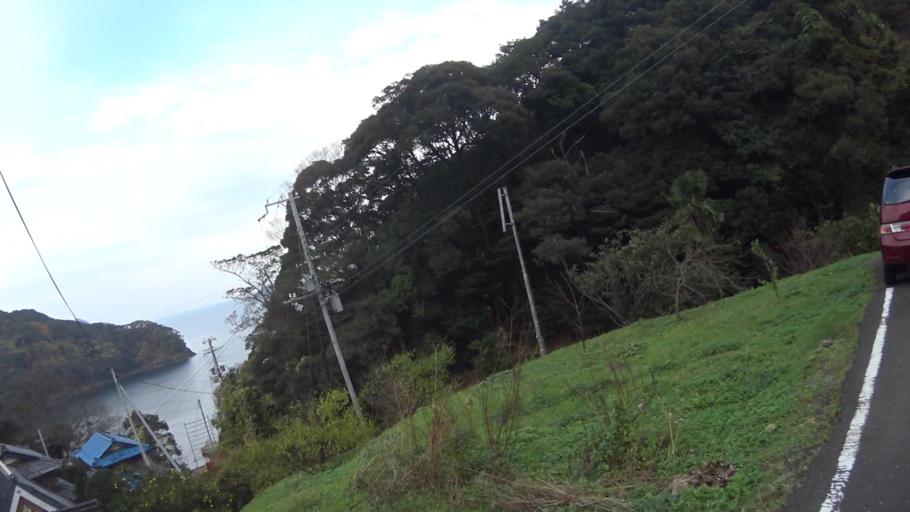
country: JP
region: Kyoto
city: Maizuru
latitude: 35.5609
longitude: 135.4685
